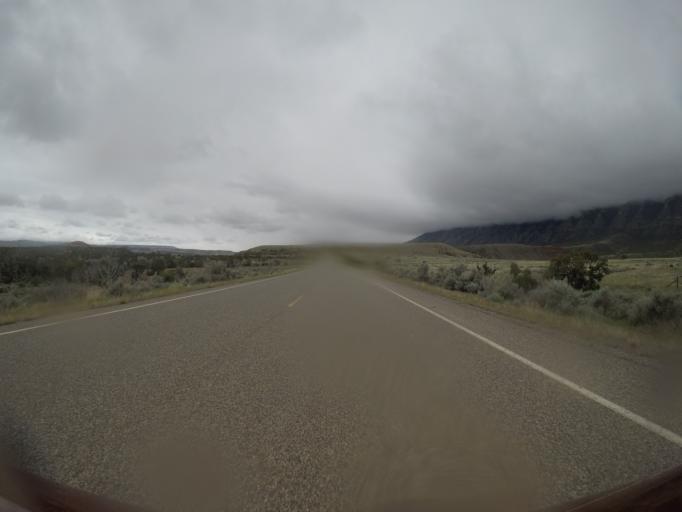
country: US
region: Wyoming
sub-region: Big Horn County
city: Lovell
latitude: 45.0897
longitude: -108.2511
